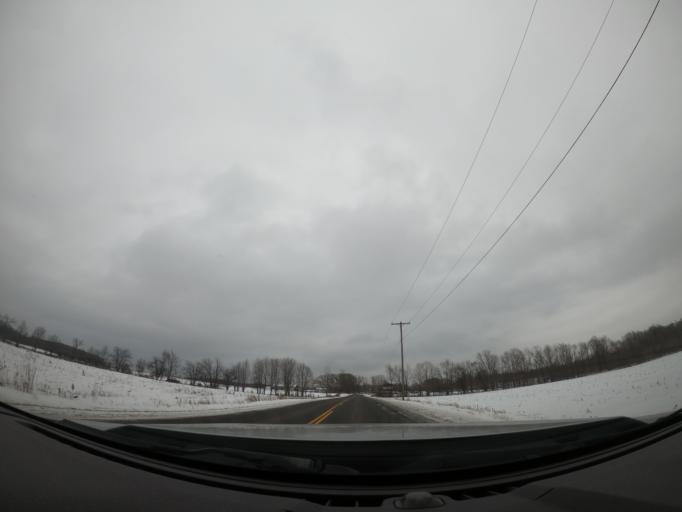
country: US
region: New York
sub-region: Cayuga County
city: Moravia
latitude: 42.7588
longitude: -76.3528
